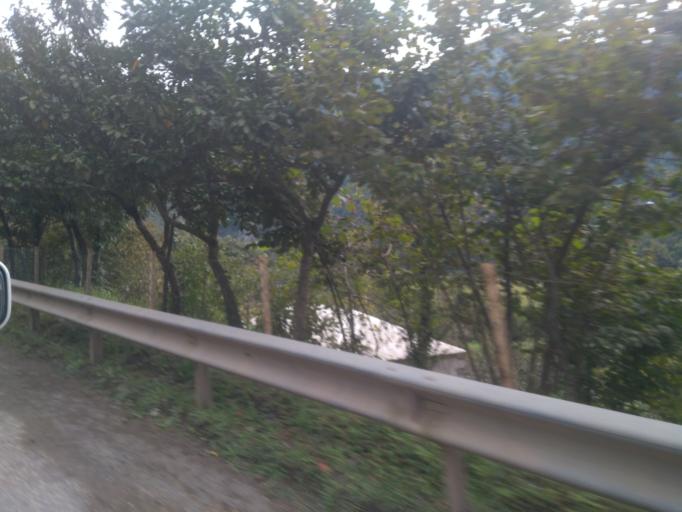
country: TR
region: Artvin
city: Muratli
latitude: 41.5455
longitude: 41.7849
